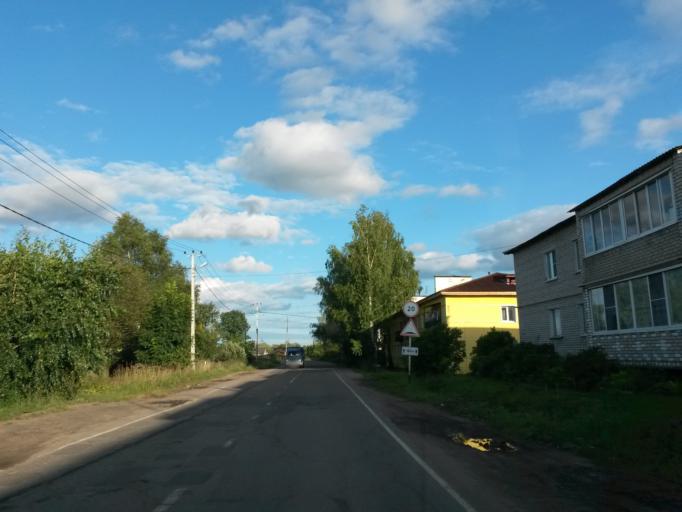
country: RU
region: Jaroslavl
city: Tutayev
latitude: 57.8786
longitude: 39.5591
